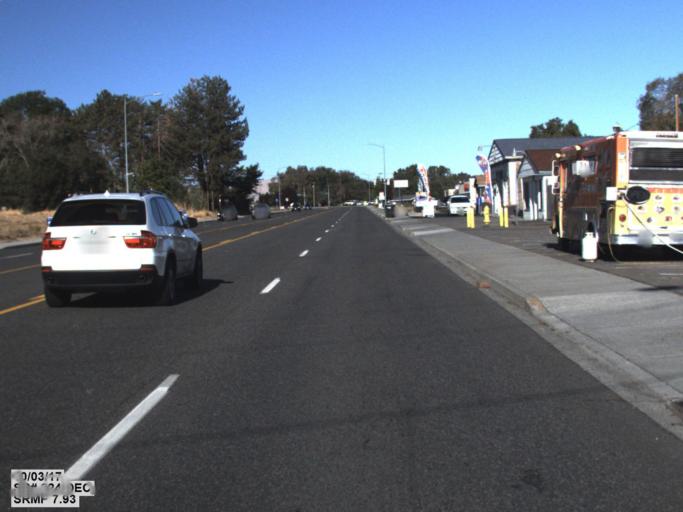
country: US
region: Washington
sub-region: Benton County
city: West Richland
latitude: 46.2986
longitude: -119.3425
